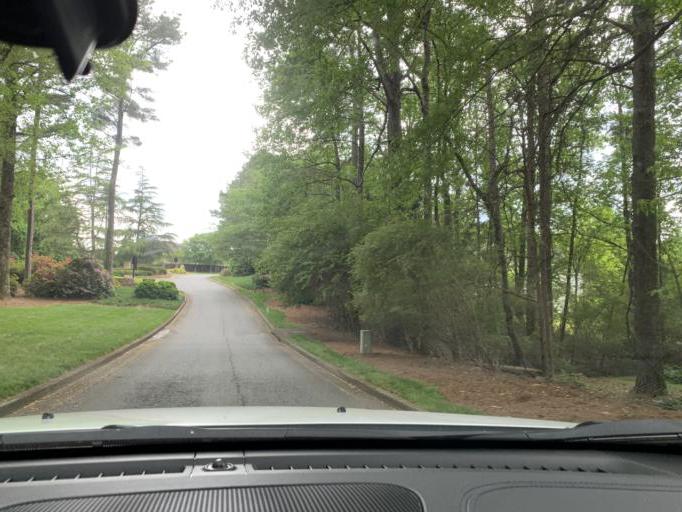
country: US
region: Georgia
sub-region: Gwinnett County
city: Suwanee
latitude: 34.1018
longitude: -84.1179
